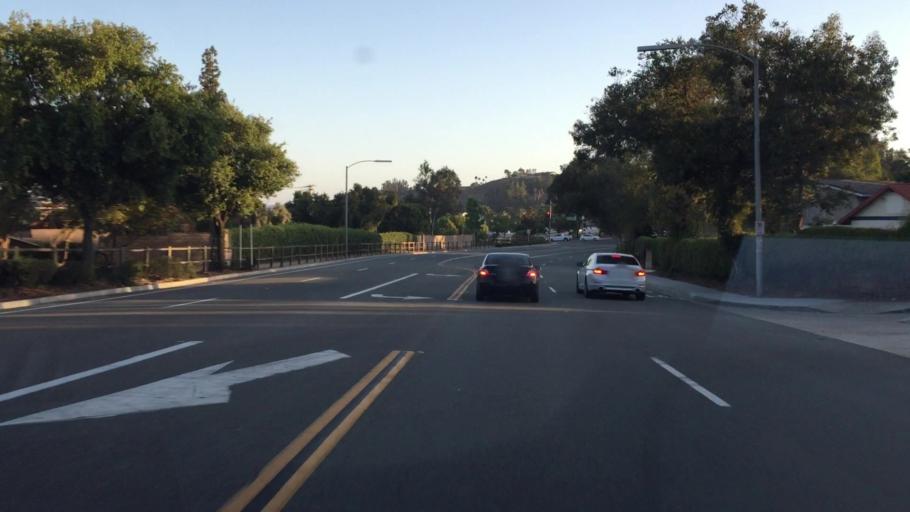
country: US
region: California
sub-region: San Diego County
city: Poway
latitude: 32.9761
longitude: -117.0396
